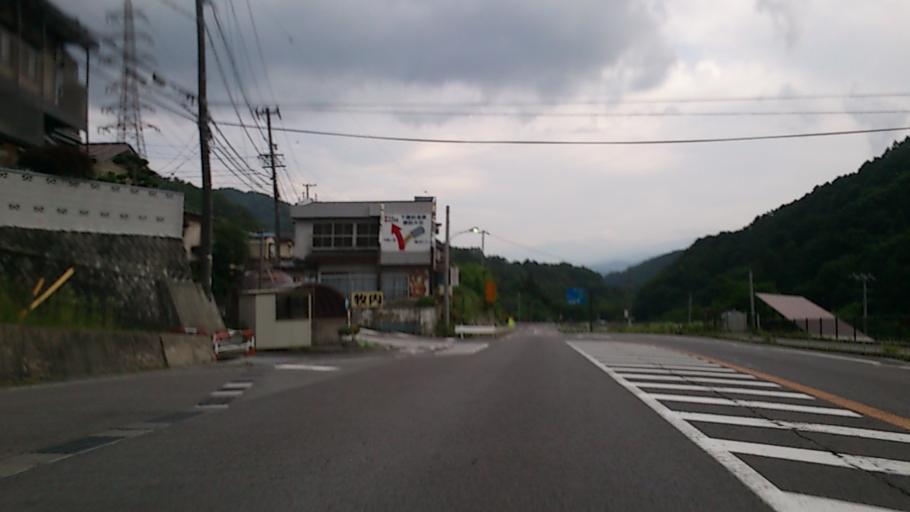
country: JP
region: Nagano
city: Suwa
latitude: 36.1052
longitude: 138.0953
